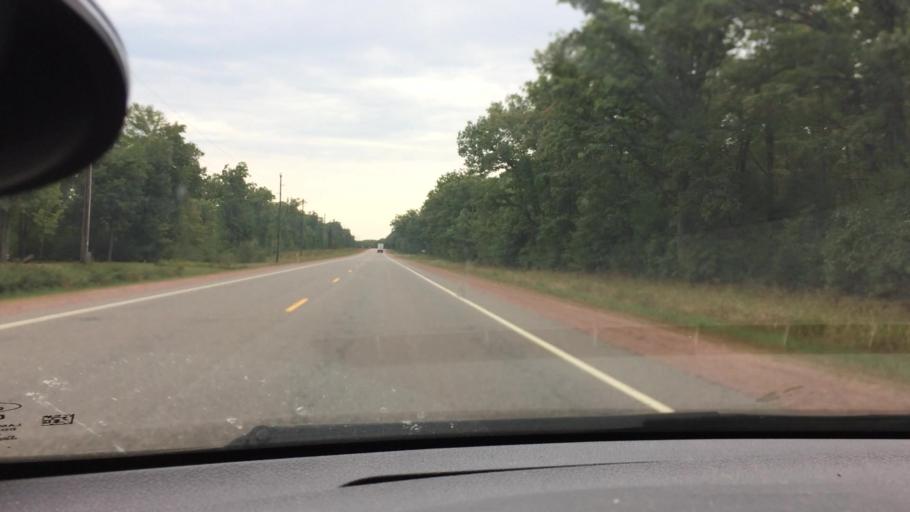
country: US
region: Wisconsin
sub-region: Clark County
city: Neillsville
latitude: 44.5761
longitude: -90.7347
